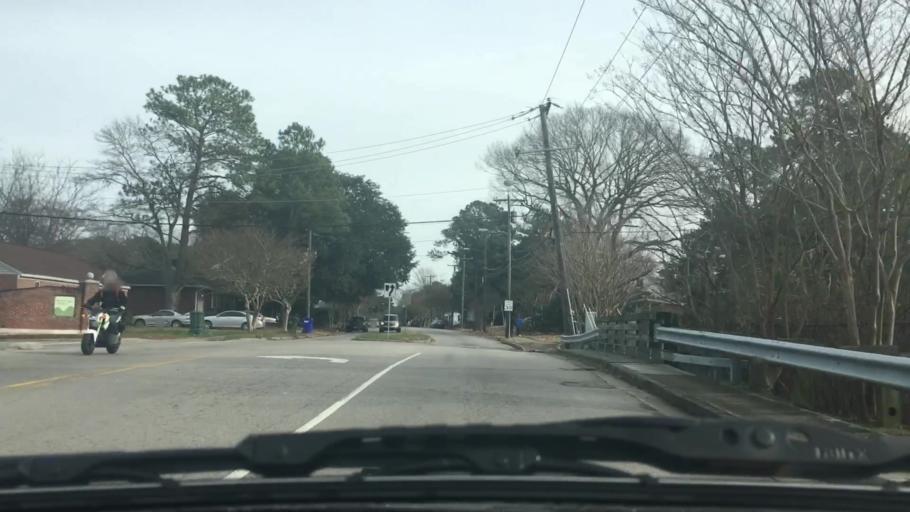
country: US
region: Virginia
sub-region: City of Norfolk
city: Norfolk
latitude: 36.8902
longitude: -76.2535
